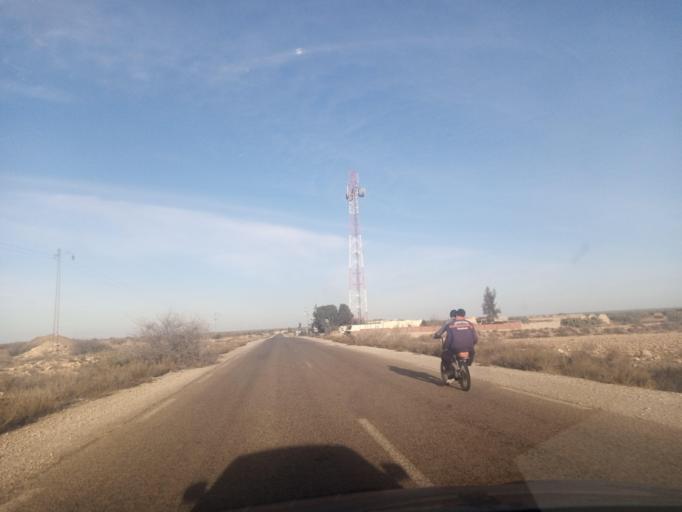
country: TN
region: Safaqis
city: Bi'r `Ali Bin Khalifah
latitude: 34.9431
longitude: 10.3470
